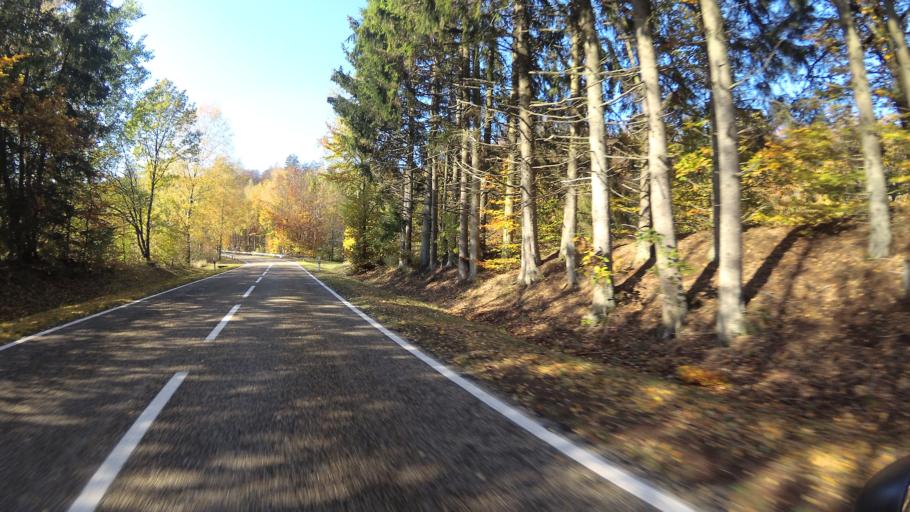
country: DE
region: Saarland
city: Losheim
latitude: 49.5519
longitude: 6.7398
